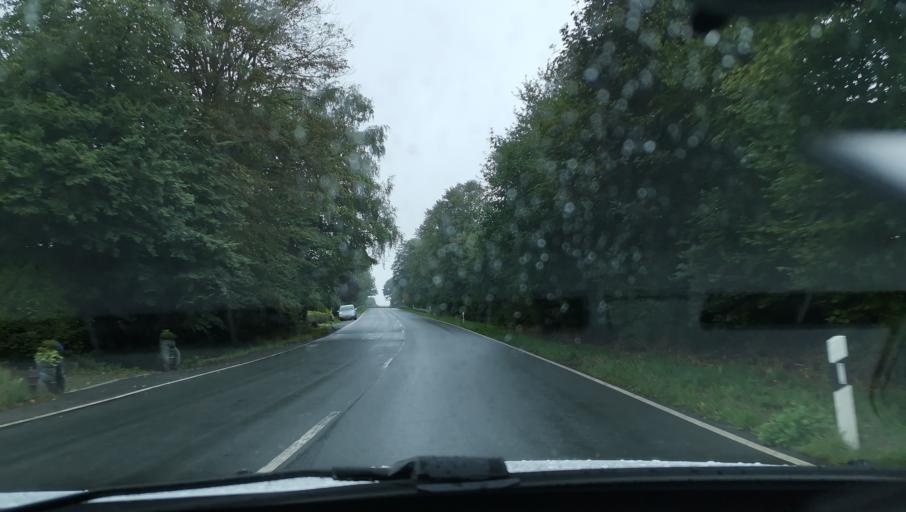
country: DE
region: North Rhine-Westphalia
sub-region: Regierungsbezirk Arnsberg
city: Breckerfeld
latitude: 51.2455
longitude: 7.4710
